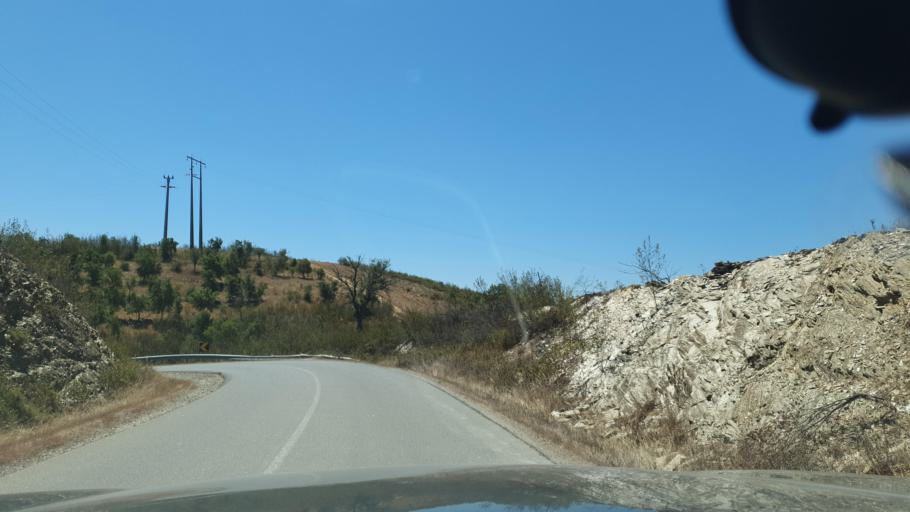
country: PT
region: Beja
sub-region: Odemira
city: Odemira
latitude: 37.5515
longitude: -8.4387
